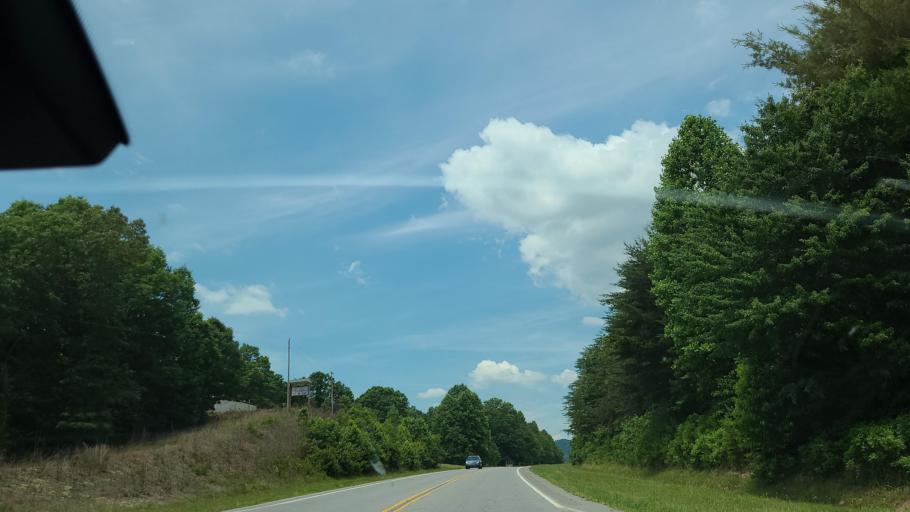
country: US
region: Georgia
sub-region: Towns County
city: Hiawassee
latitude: 35.0278
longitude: -83.7207
